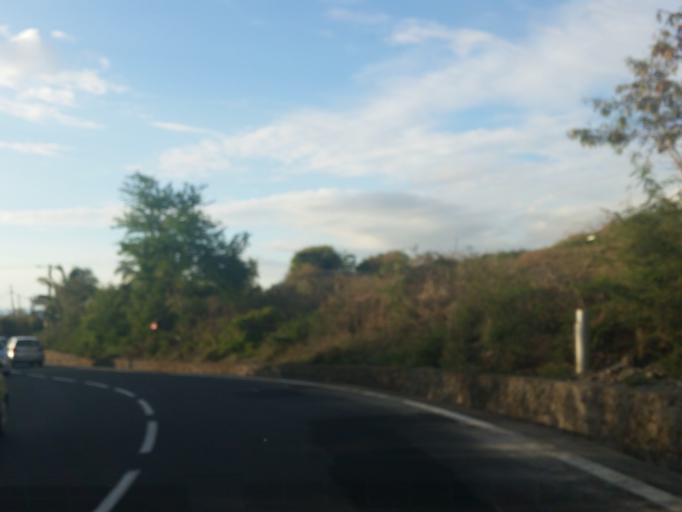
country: RE
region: Reunion
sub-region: Reunion
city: Saint-Leu
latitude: -21.1402
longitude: 55.2829
